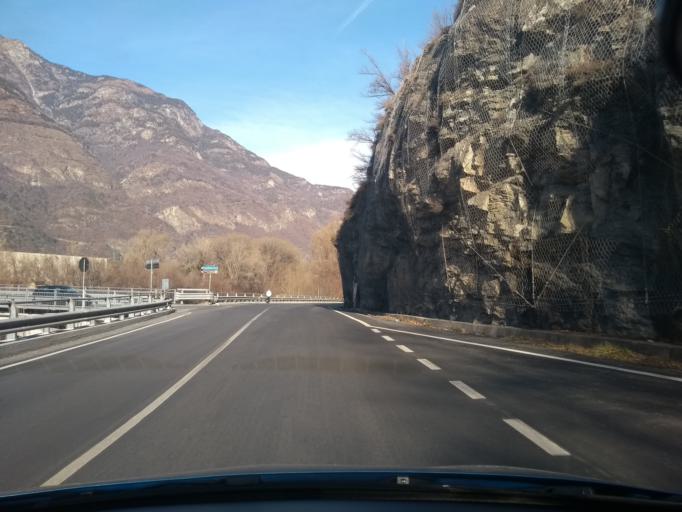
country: IT
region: Aosta Valley
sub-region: Valle d'Aosta
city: Champdepraz
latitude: 45.6815
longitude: 7.6747
